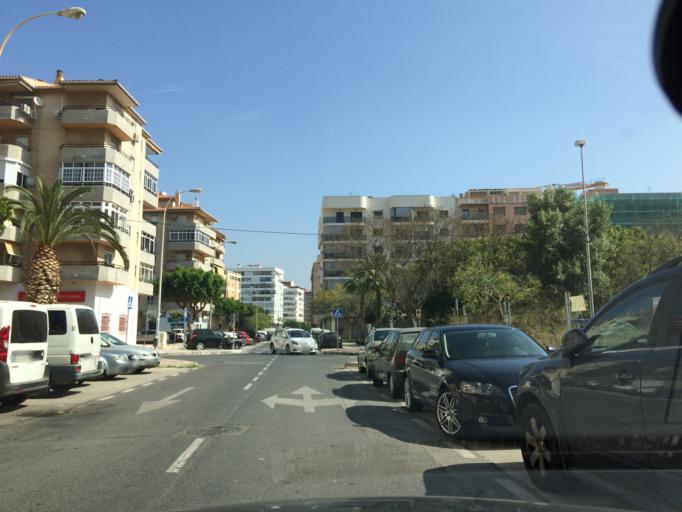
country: ES
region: Andalusia
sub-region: Provincia de Malaga
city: Malaga
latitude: 36.6932
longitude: -4.4438
